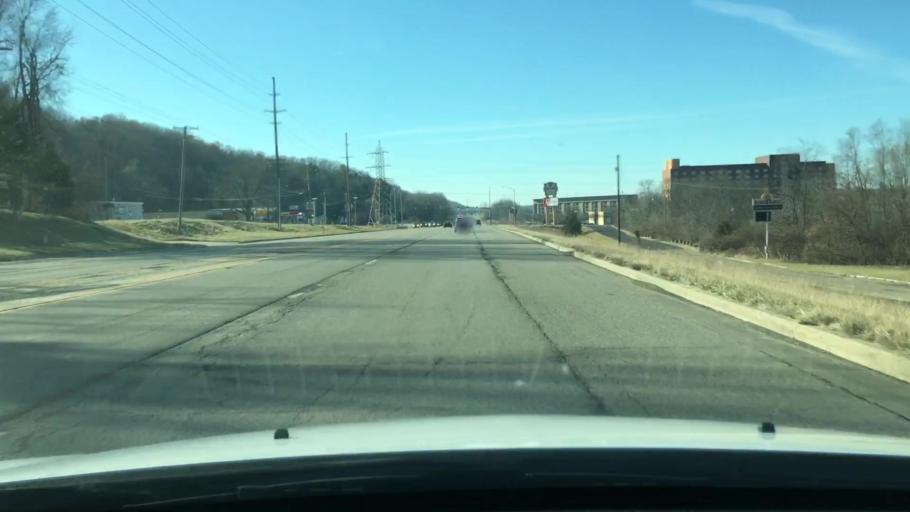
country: US
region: Illinois
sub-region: Tazewell County
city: East Peoria
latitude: 40.6795
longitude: -89.5584
